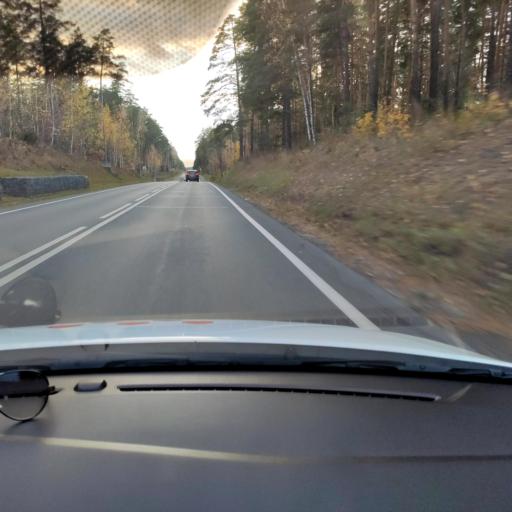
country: RU
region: Tatarstan
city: Verkhniy Uslon
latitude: 55.6378
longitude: 49.0478
